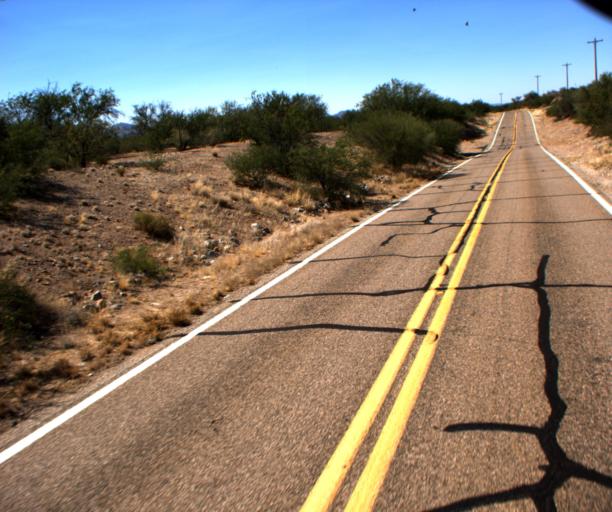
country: US
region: Arizona
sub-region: Pima County
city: Three Points
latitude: 31.8733
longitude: -111.3952
